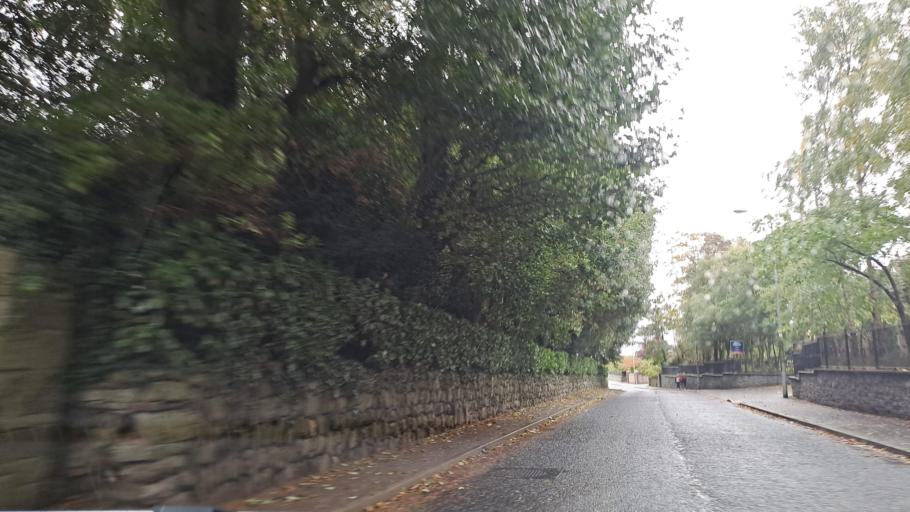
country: IE
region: Leinster
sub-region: Lu
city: Blackrock
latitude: 53.9597
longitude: -6.3757
